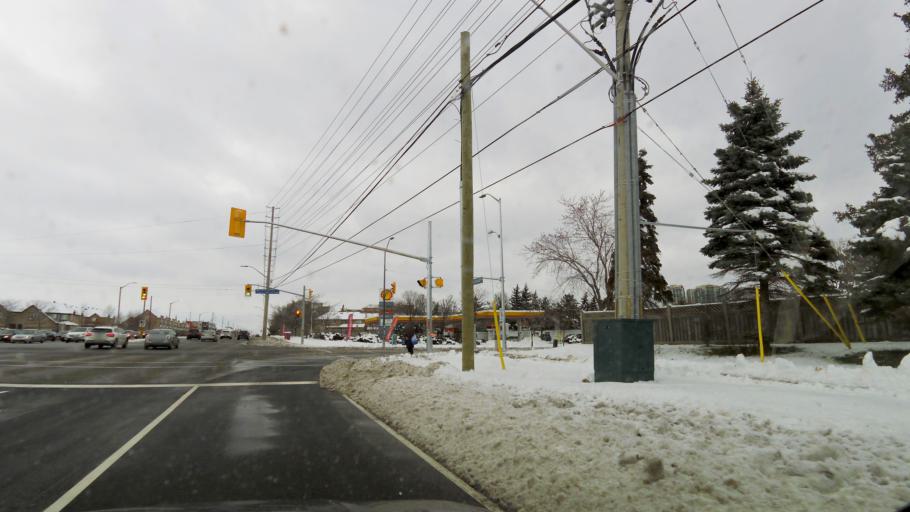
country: CA
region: Ontario
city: Mississauga
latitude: 43.5467
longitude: -79.7140
